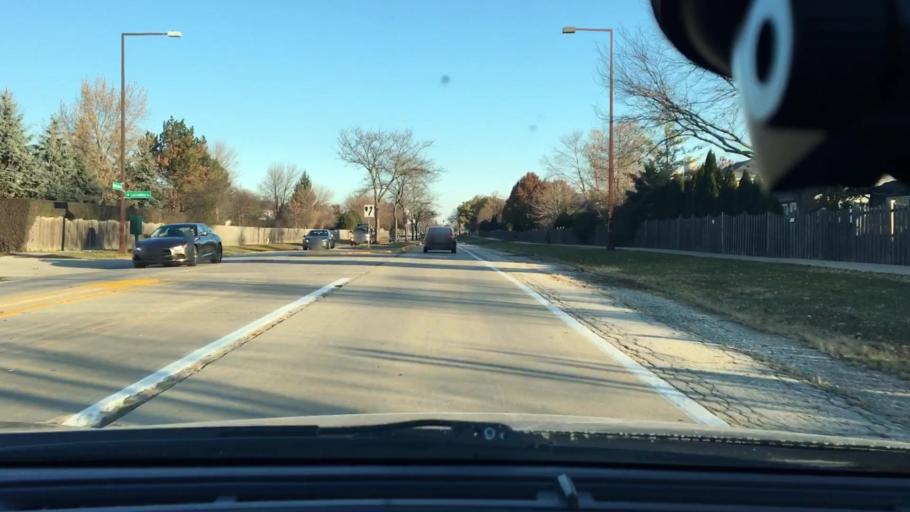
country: US
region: Illinois
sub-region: Cook County
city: Buffalo Grove
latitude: 42.1749
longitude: -87.9652
